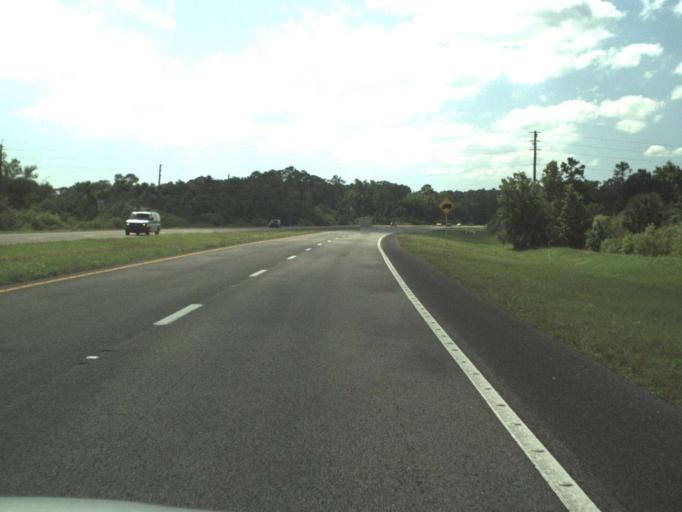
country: US
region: Florida
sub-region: Orange County
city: Christmas
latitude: 28.3895
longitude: -80.9372
